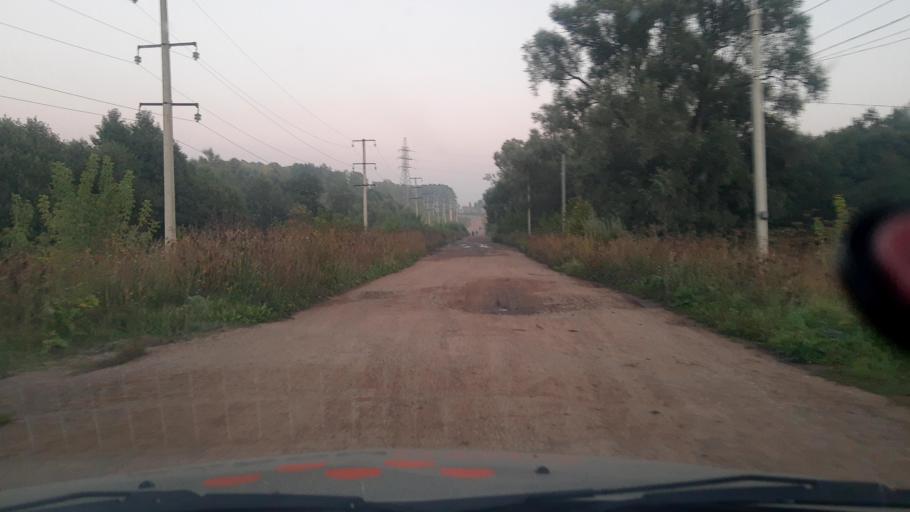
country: RU
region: Bashkortostan
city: Blagoveshchensk
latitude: 55.0496
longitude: 55.9830
